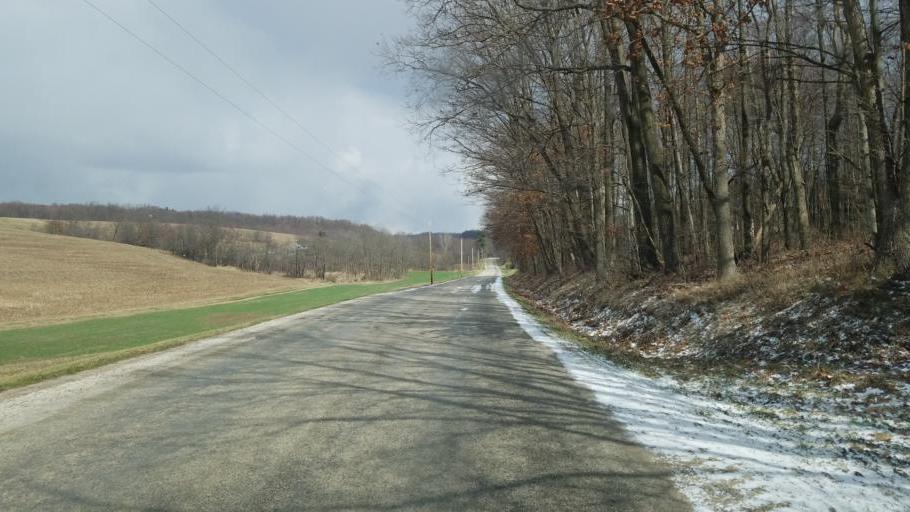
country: US
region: Ohio
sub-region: Tuscarawas County
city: Sugarcreek
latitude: 40.4439
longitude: -81.6714
